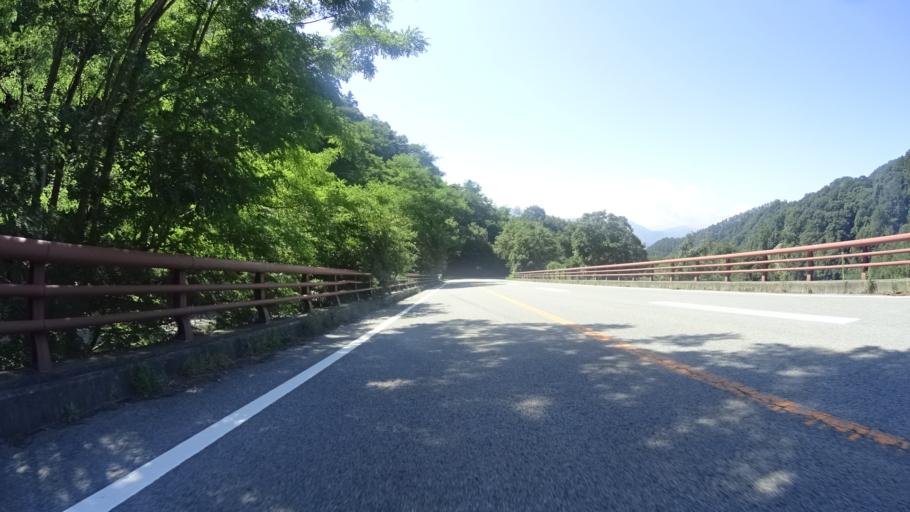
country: JP
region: Yamanashi
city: Enzan
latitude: 35.7628
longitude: 138.8067
